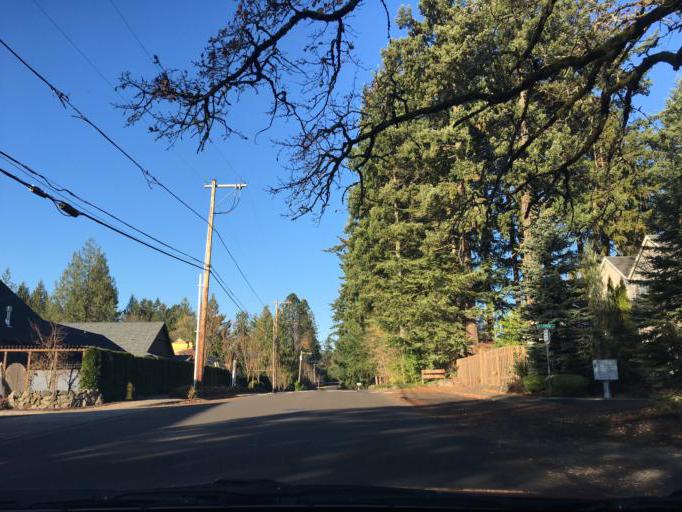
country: US
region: Oregon
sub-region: Washington County
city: Raleigh Hills
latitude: 45.4879
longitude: -122.7758
